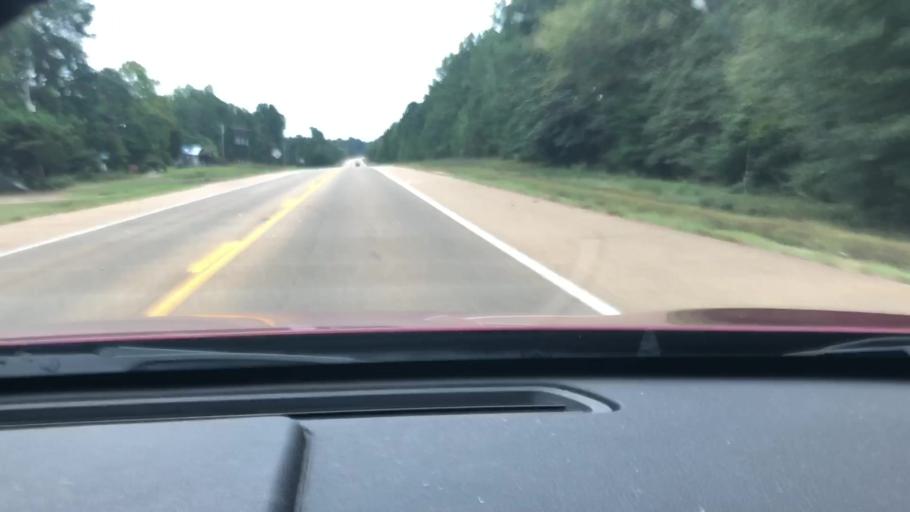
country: US
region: Arkansas
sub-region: Lafayette County
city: Stamps
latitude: 33.3590
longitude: -93.4242
